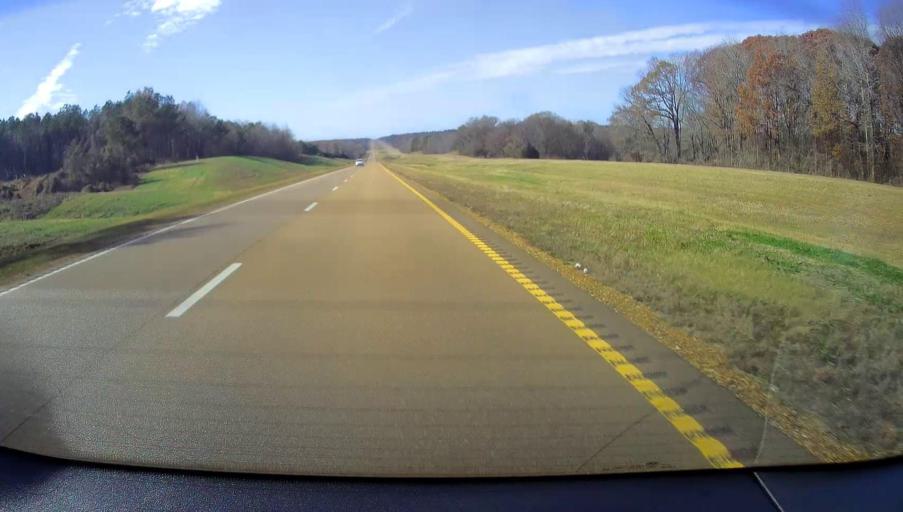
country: US
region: Mississippi
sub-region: Benton County
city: Ashland
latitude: 34.9532
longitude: -89.0435
